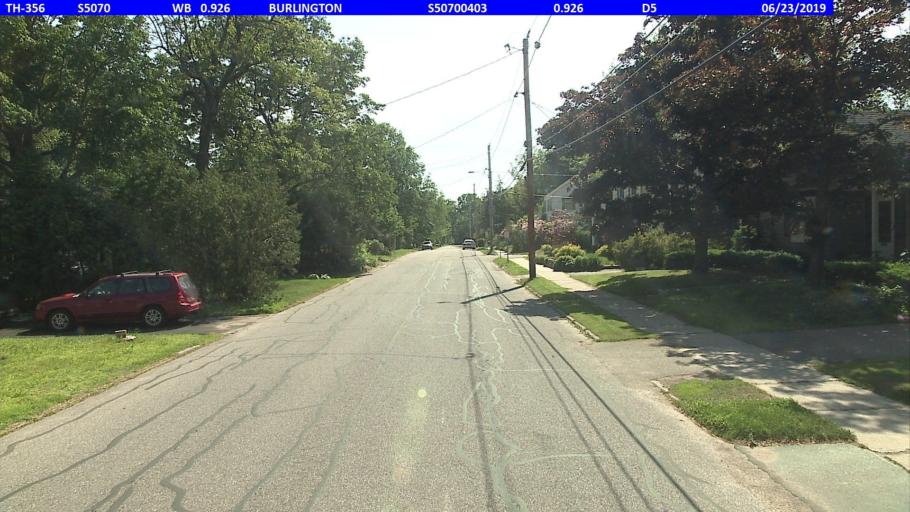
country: US
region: Vermont
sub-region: Chittenden County
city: Burlington
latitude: 44.5097
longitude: -73.2573
